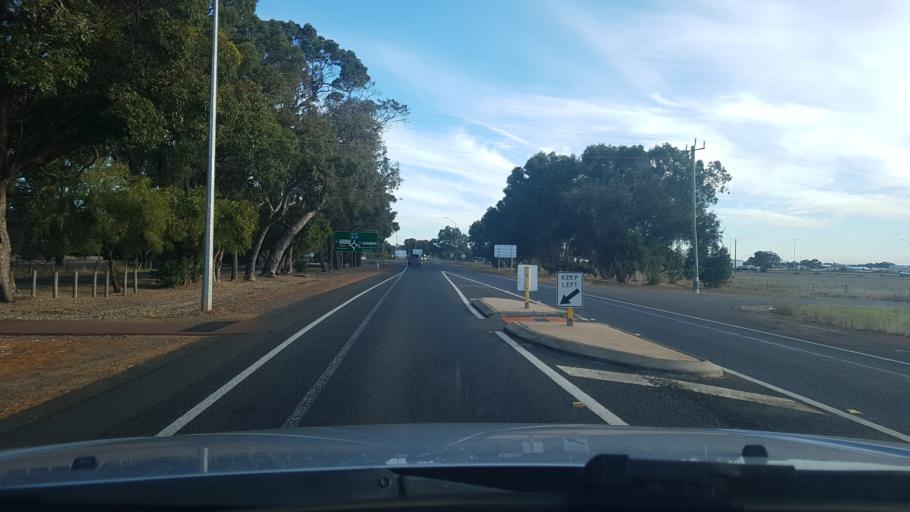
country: AU
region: Western Australia
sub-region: Busselton
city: Vasse
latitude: -33.6724
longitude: 115.2550
